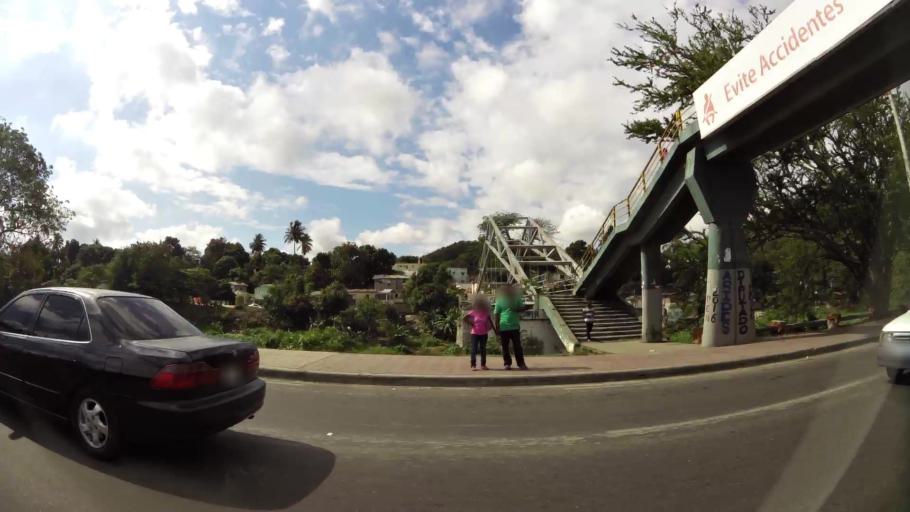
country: DO
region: Santiago
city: Santiago de los Caballeros
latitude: 19.4487
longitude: -70.7112
